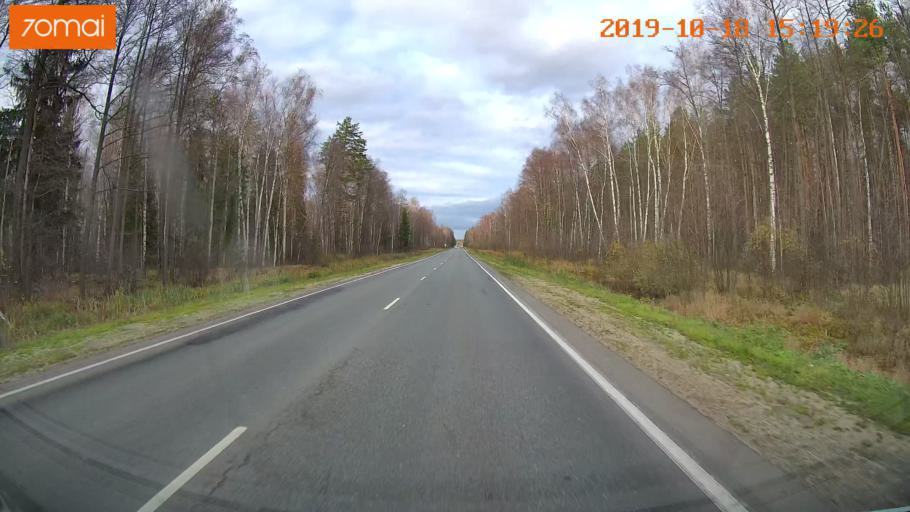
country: RU
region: Vladimir
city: Anopino
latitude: 55.6730
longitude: 40.7377
